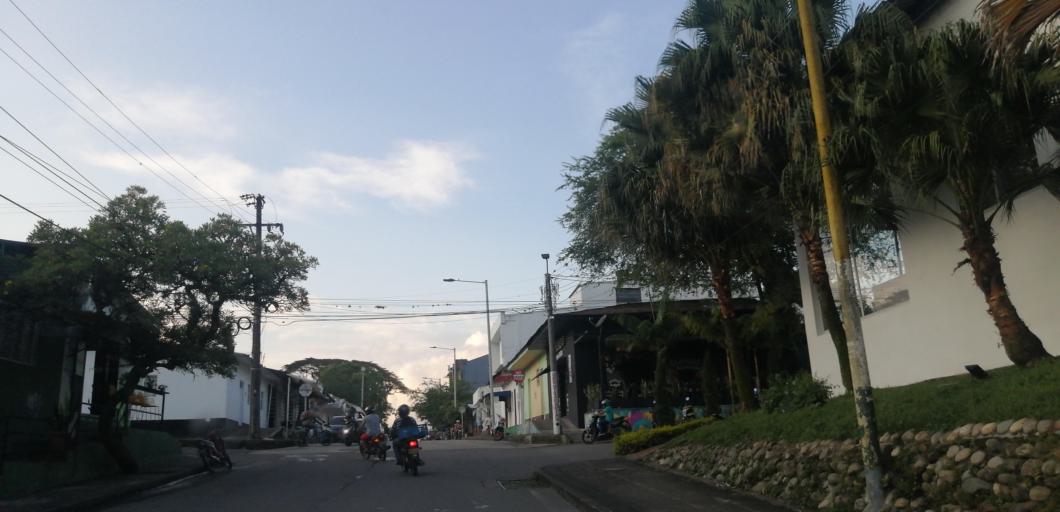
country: CO
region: Meta
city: Acacias
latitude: 3.9840
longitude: -73.7578
